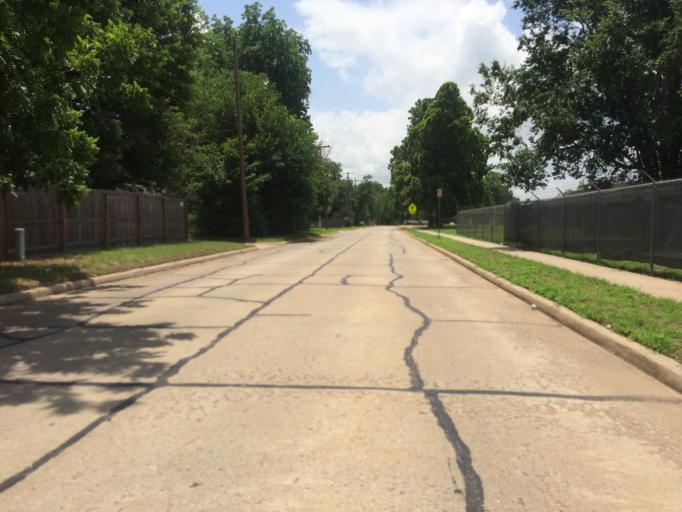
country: US
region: Oklahoma
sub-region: Cleveland County
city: Norman
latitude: 35.2138
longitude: -97.4690
